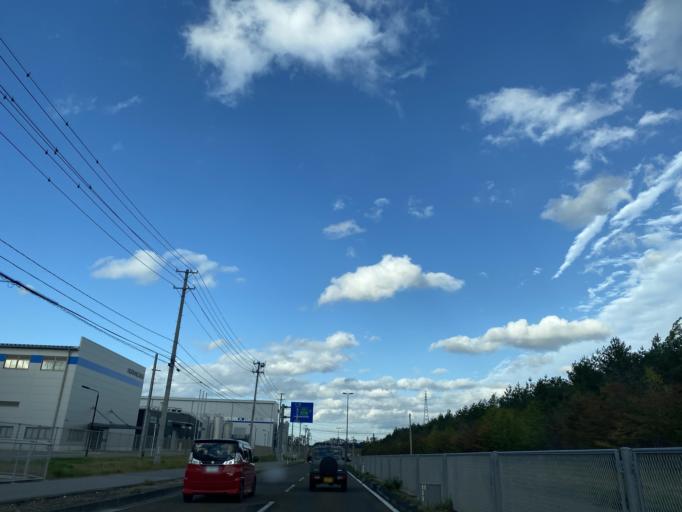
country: JP
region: Miyagi
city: Tomiya
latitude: 38.3666
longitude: 140.8528
